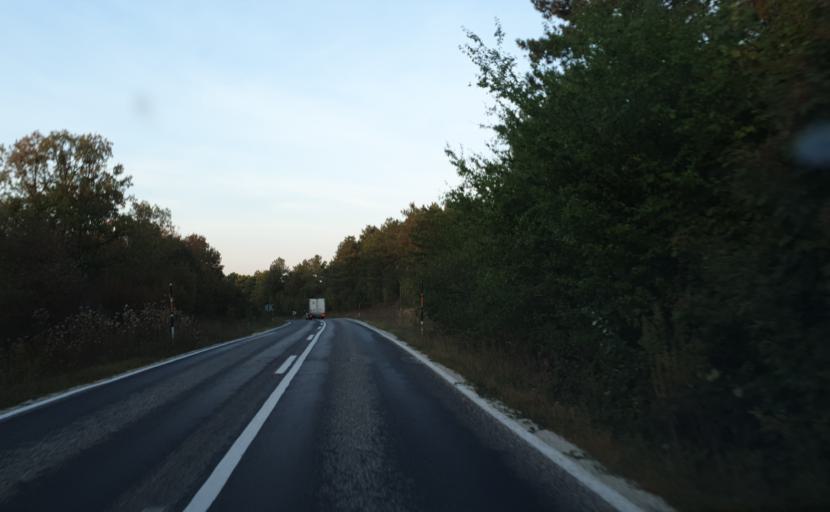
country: TR
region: Kirklareli
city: Igneada
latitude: 41.8657
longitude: 27.8854
